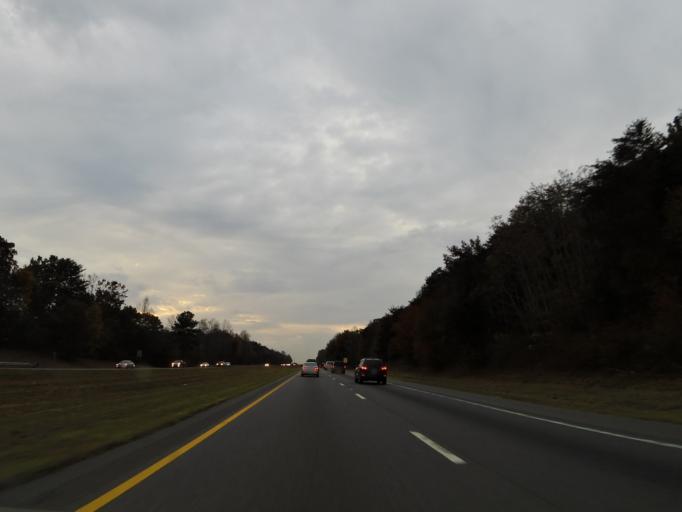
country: US
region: North Carolina
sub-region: Burke County
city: Hildebran
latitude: 35.7059
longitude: -81.4054
